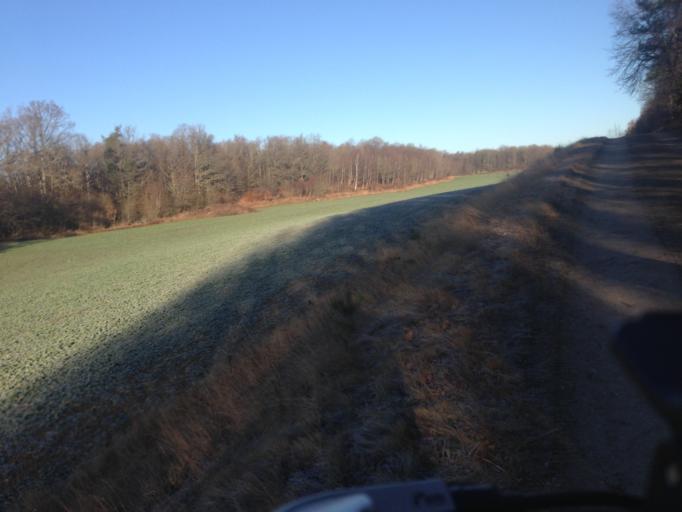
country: SE
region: Blekinge
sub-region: Karlshamns Kommun
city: Morrum
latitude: 56.1816
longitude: 14.7822
